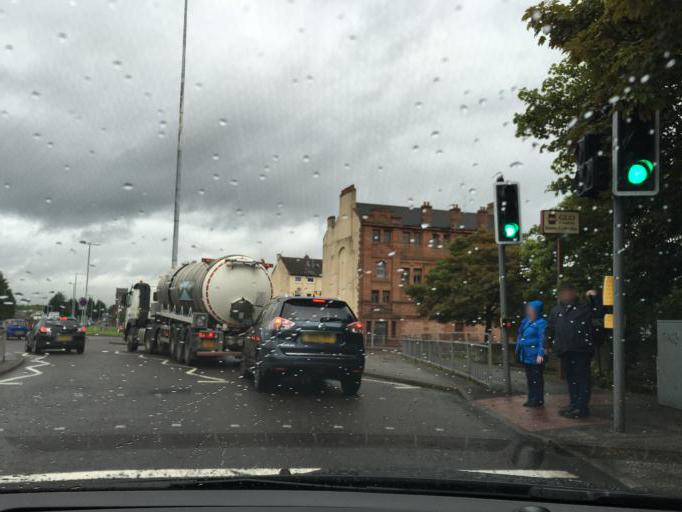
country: GB
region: Scotland
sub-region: North Lanarkshire
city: Motherwell
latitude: 55.7917
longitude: -3.9937
